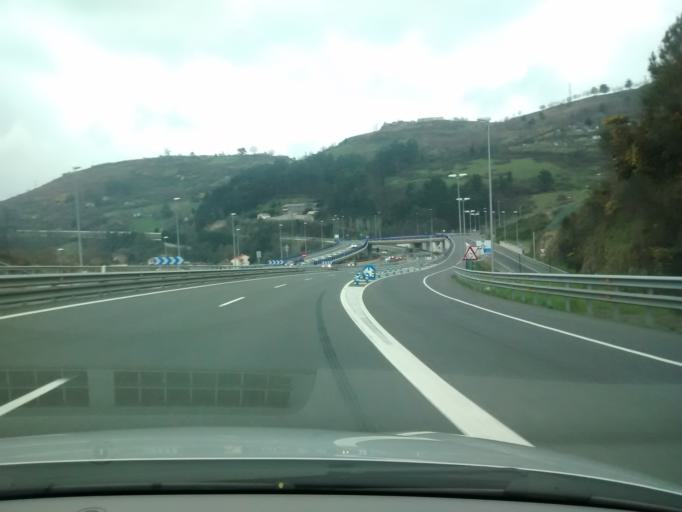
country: ES
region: Basque Country
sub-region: Bizkaia
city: Alonsotegi
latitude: 43.2537
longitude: -2.9727
